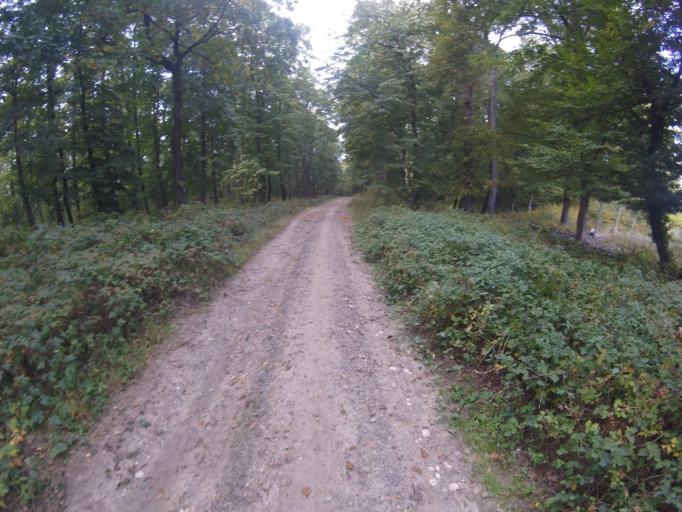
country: HU
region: Komarom-Esztergom
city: Kesztolc
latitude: 47.7716
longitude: 18.8138
